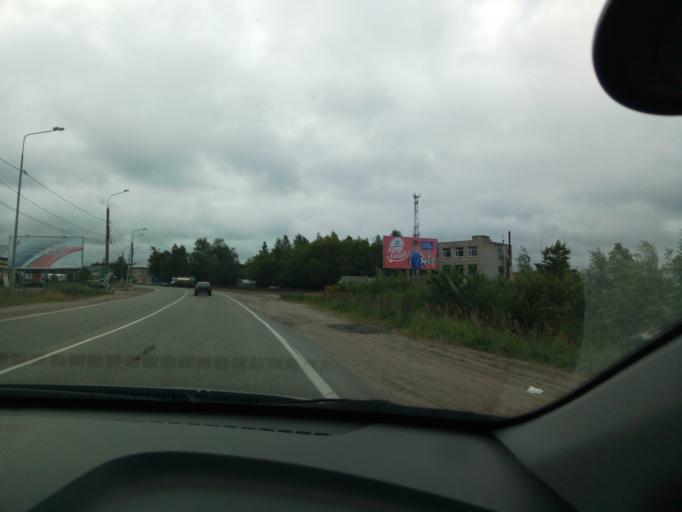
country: RU
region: Chuvashia
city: Shumerlya
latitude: 55.4865
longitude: 46.4388
